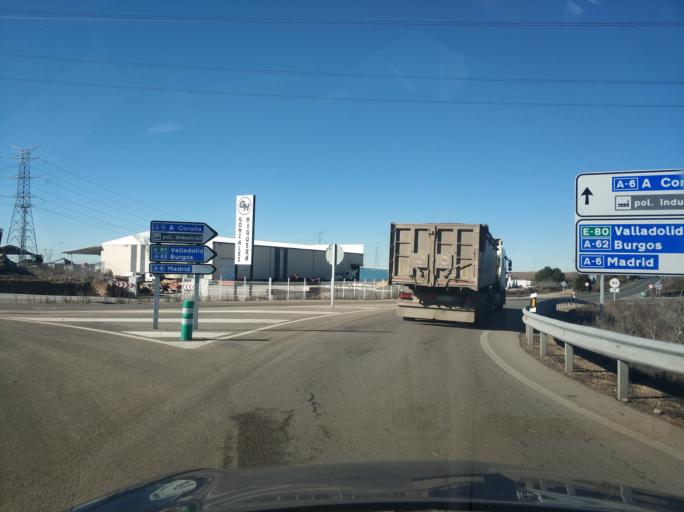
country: ES
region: Castille and Leon
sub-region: Provincia de Valladolid
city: Tordesillas
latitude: 41.5088
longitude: -5.0139
